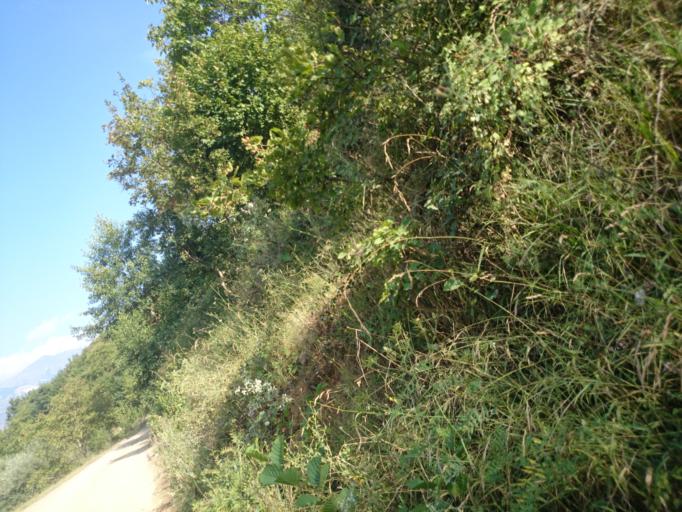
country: AL
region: Diber
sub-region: Rrethi i Dibres
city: Arras
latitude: 41.7368
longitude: 20.3029
